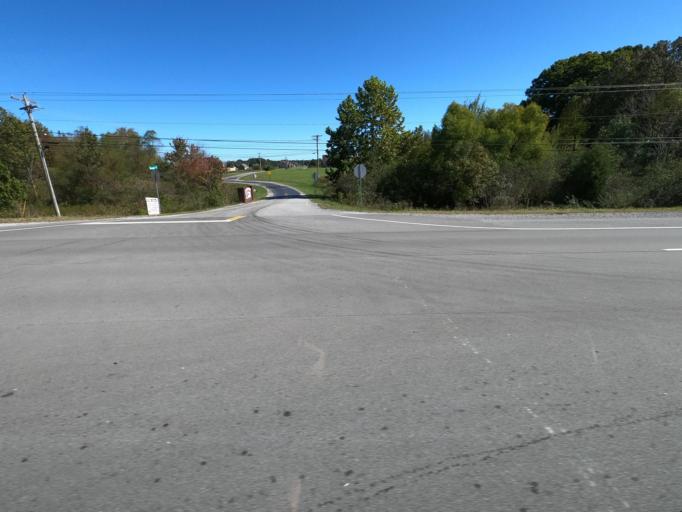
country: US
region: Tennessee
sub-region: Maury County
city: Mount Pleasant
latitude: 35.4269
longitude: -87.2817
